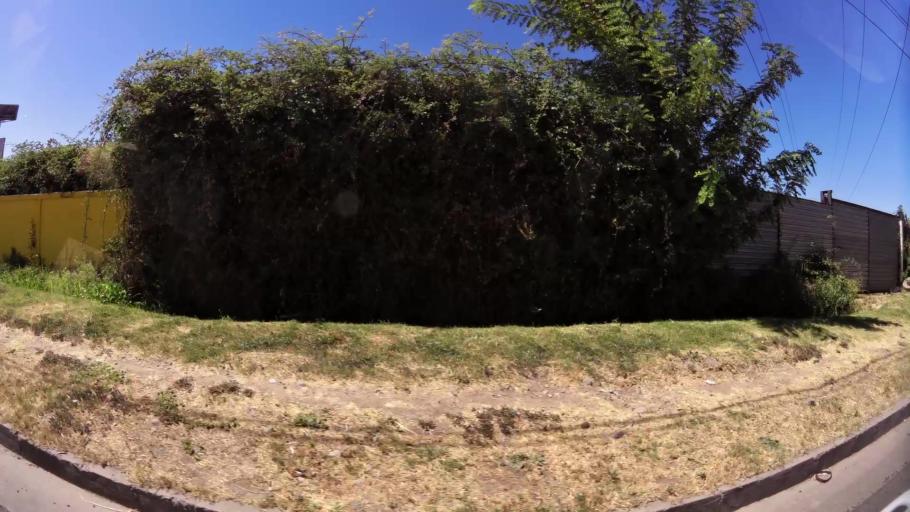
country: CL
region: O'Higgins
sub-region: Provincia de Cachapoal
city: Rancagua
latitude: -34.1529
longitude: -70.7258
